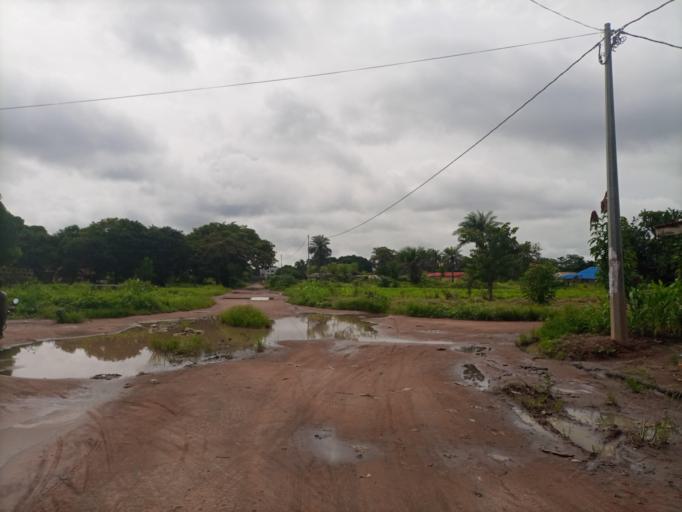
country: SL
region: Northern Province
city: Sawkta
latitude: 8.6244
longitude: -13.2042
